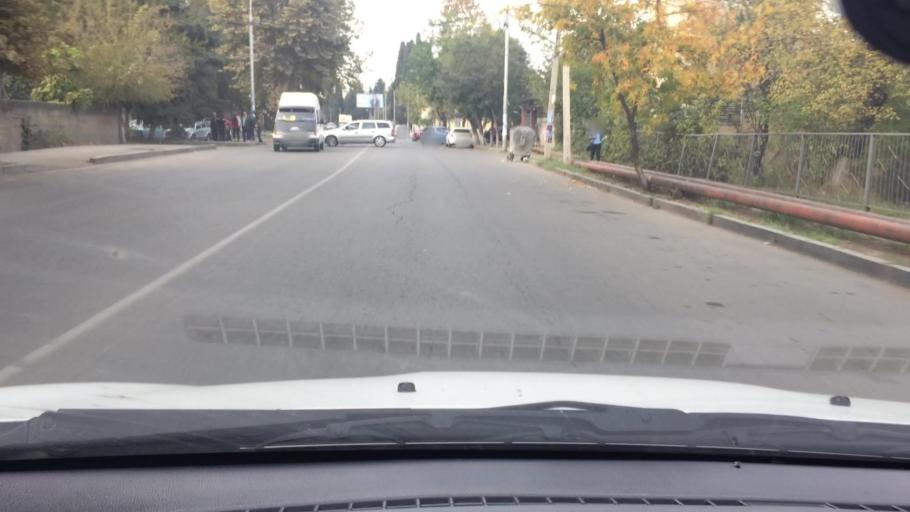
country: GE
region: Kvemo Kartli
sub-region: Marneuli
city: Marneuli
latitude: 41.4707
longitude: 44.8163
